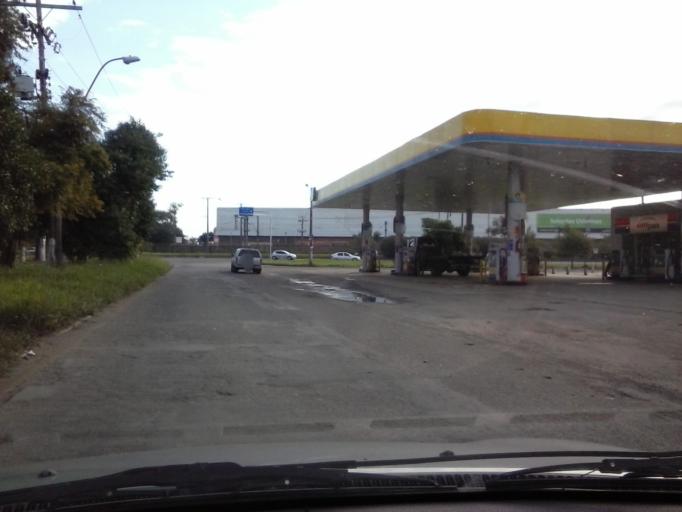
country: BR
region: Rio Grande do Sul
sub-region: Canoas
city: Canoas
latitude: -29.9753
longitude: -51.1770
